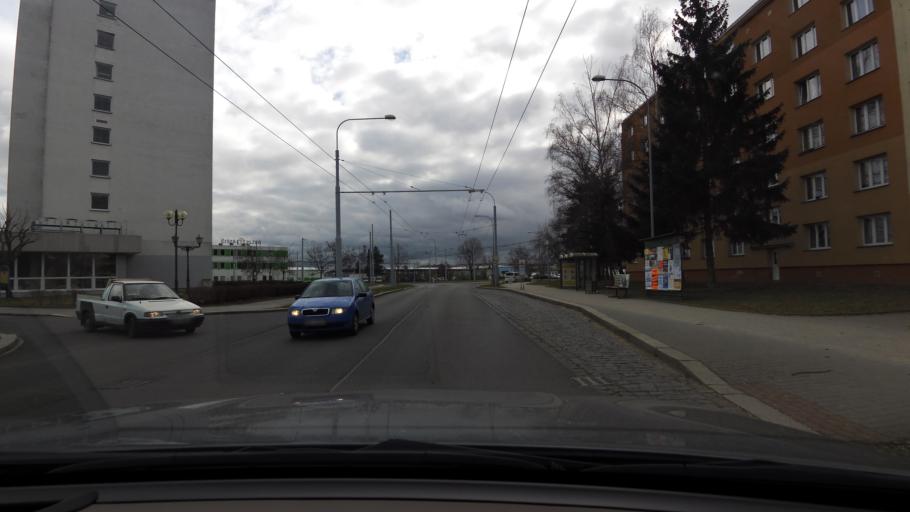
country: CZ
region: Plzensky
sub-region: Okres Plzen-Mesto
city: Pilsen
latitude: 49.7262
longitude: 13.3761
